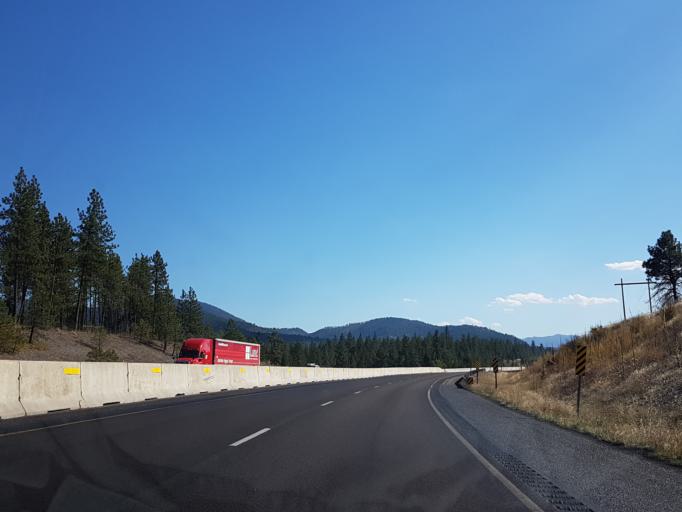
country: US
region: Montana
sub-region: Mineral County
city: Superior
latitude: 47.1335
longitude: -114.7984
